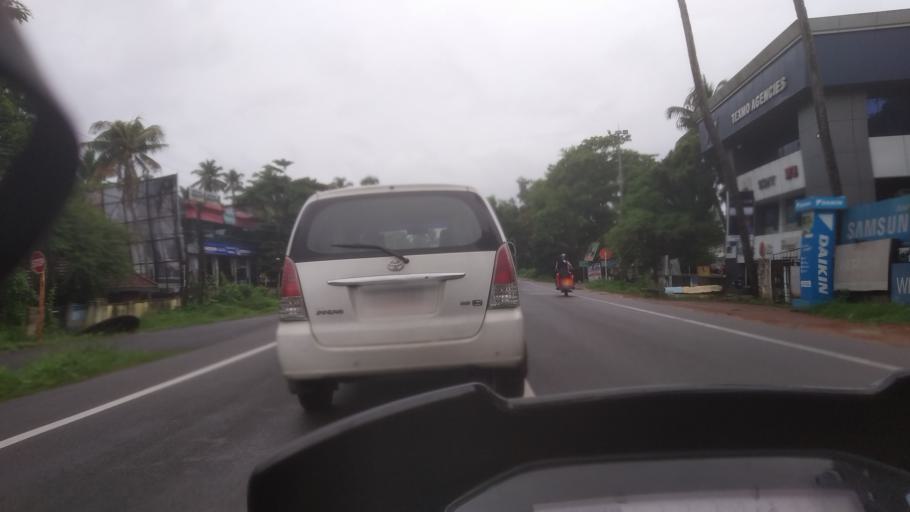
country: IN
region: Kerala
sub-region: Alappuzha
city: Kayankulam
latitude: 9.1656
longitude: 76.5019
